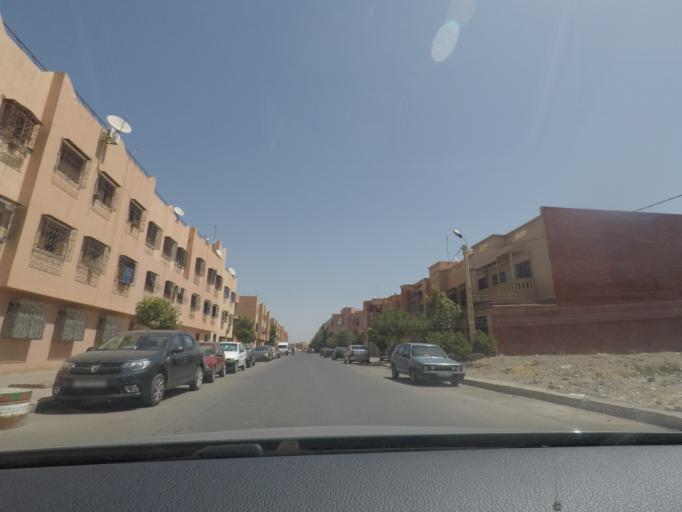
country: MA
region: Marrakech-Tensift-Al Haouz
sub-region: Marrakech
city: Marrakesh
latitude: 31.5936
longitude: -8.0283
